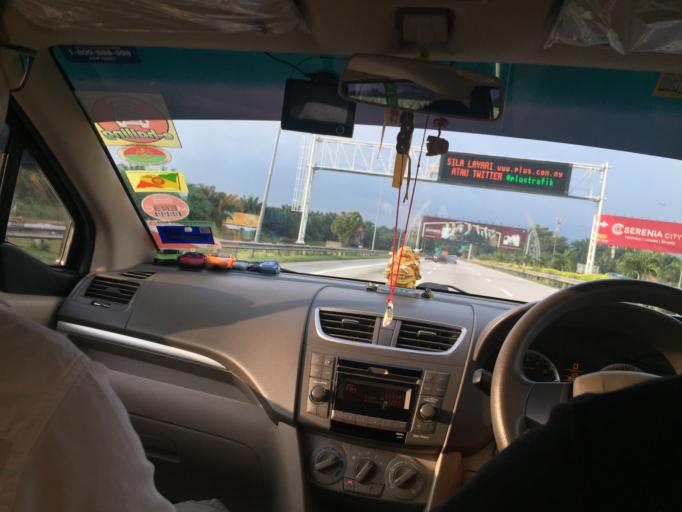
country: MY
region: Putrajaya
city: Putrajaya
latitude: 2.8403
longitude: 101.6597
